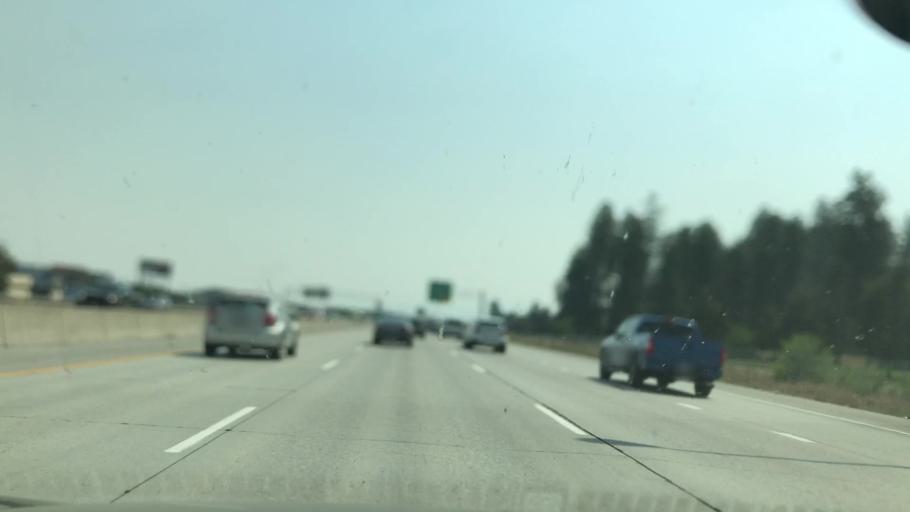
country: US
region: Washington
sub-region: Spokane County
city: Spokane Valley
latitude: 47.6739
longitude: -117.2314
